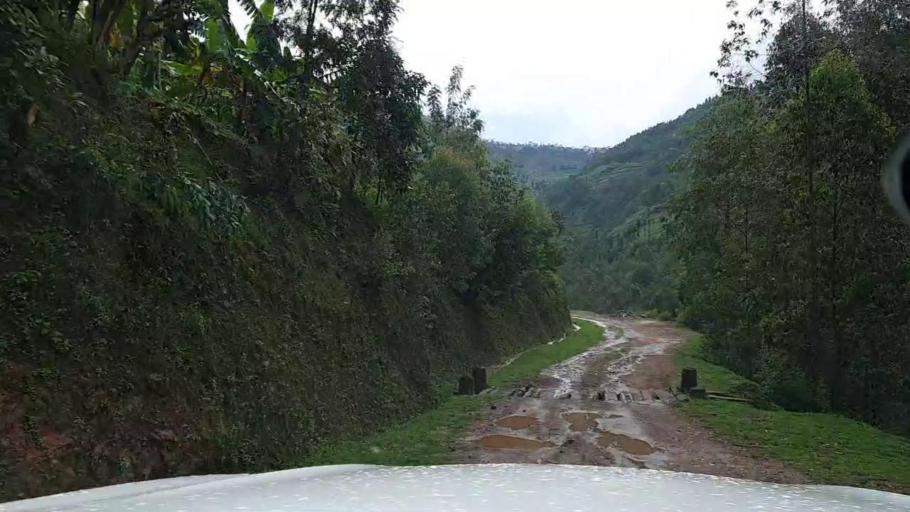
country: RW
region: Northern Province
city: Byumba
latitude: -1.7210
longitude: 29.9136
